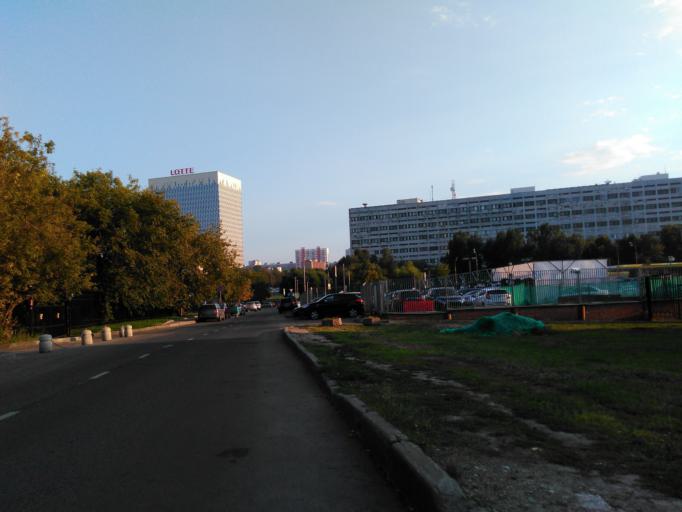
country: RU
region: Moskovskaya
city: Cheremushki
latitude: 55.6574
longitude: 37.5379
